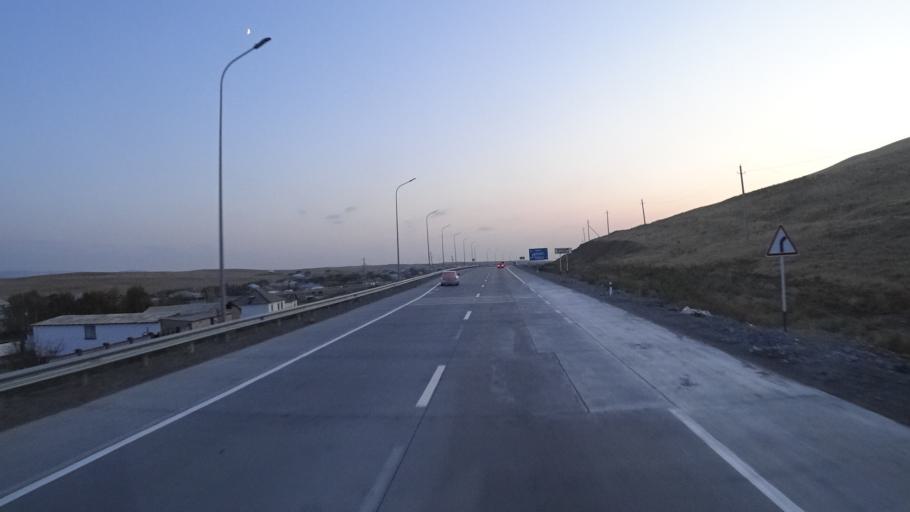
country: KZ
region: Ongtustik Qazaqstan
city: Qazyqurt
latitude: 41.8992
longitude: 69.4544
